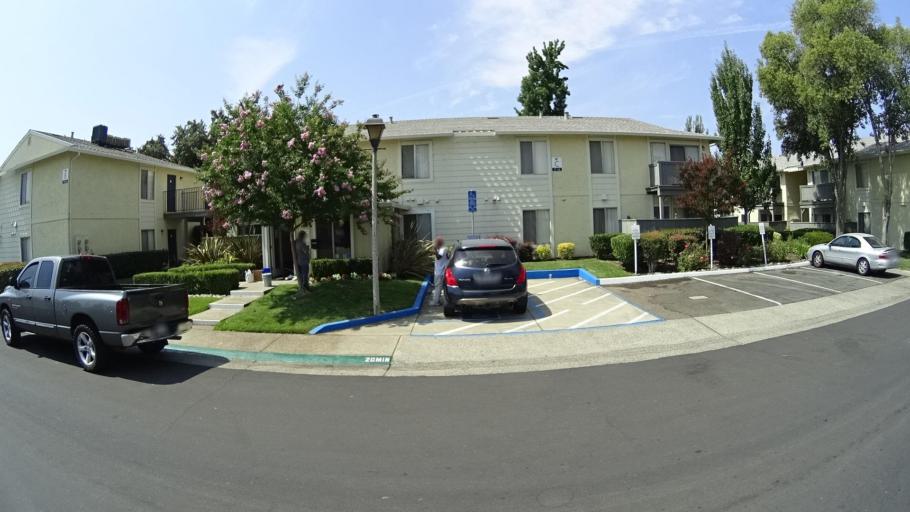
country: US
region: California
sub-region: Placer County
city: Rocklin
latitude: 38.7862
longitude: -121.2476
